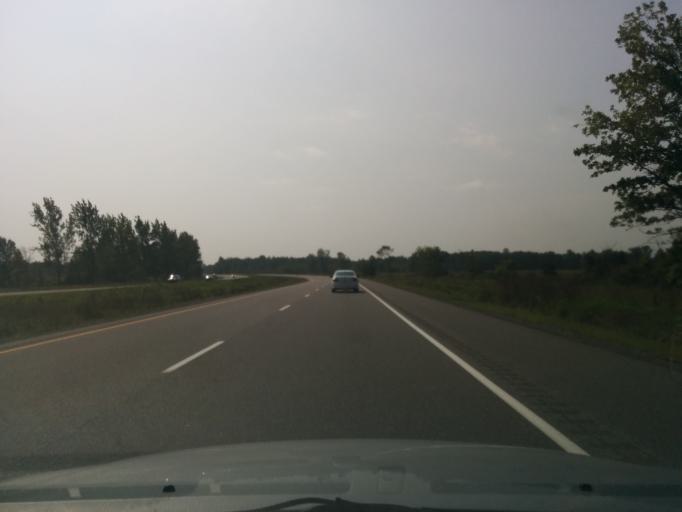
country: CA
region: Ontario
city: Bells Corners
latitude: 45.1223
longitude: -75.6759
